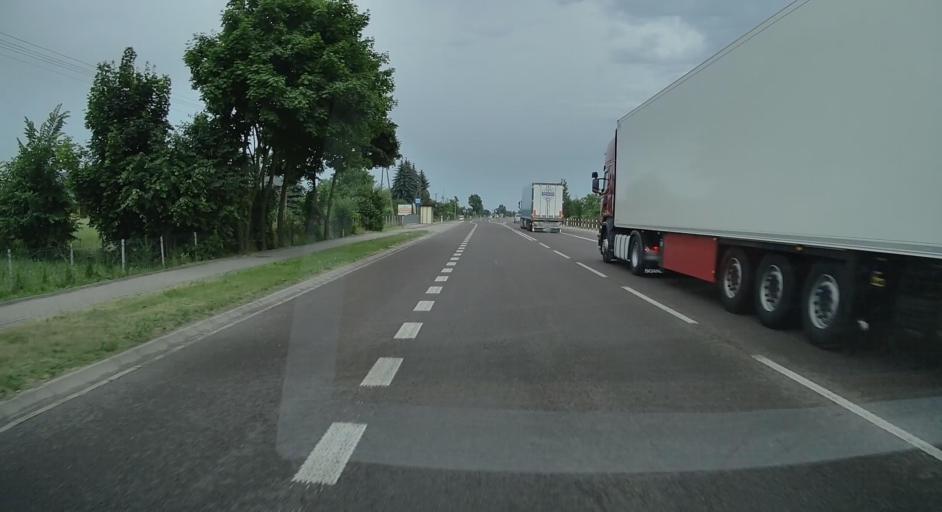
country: PL
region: Lublin Voivodeship
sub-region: Powiat bialski
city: Rzeczyca
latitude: 52.0335
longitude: 22.7011
